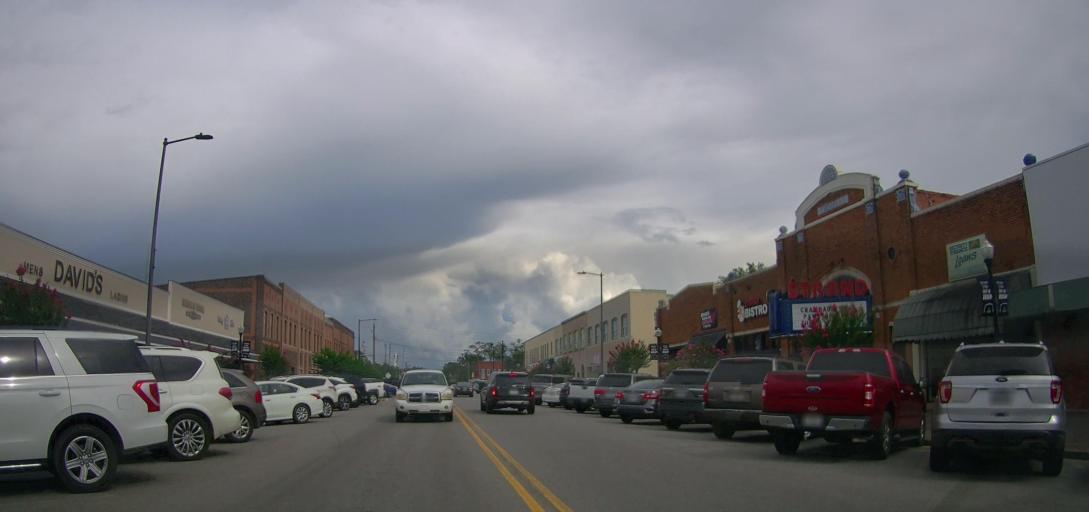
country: US
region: Georgia
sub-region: Wayne County
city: Jesup
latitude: 31.6058
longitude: -81.8841
